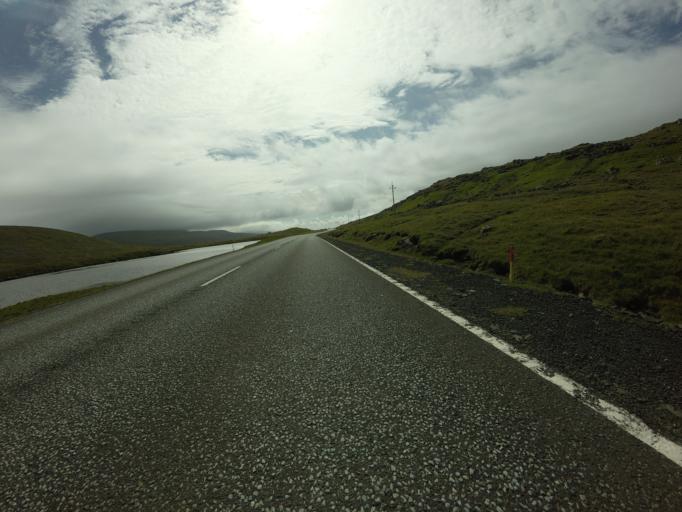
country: FO
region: Sandoy
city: Sandur
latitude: 61.8803
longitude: -6.8646
